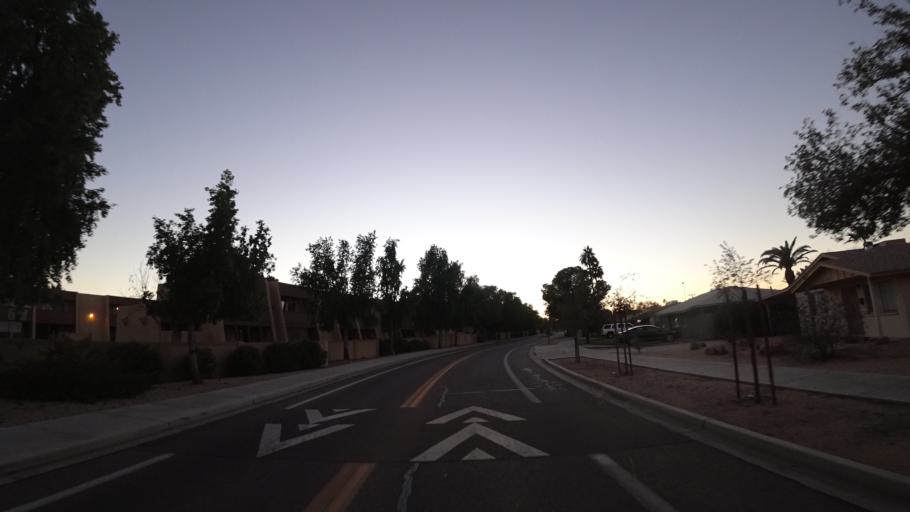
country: US
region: Arizona
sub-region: Maricopa County
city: Tempe Junction
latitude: 33.4145
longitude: -111.9487
